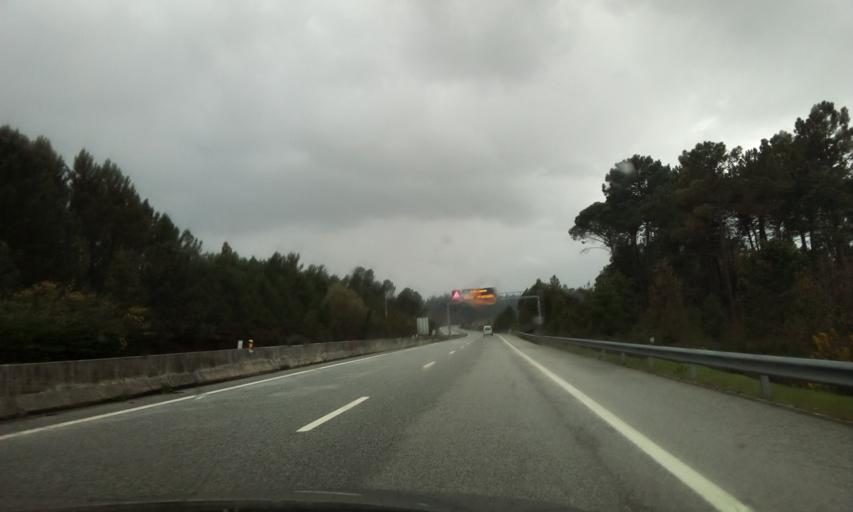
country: PT
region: Viseu
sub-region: Viseu
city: Rio de Loba
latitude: 40.6369
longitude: -7.8803
